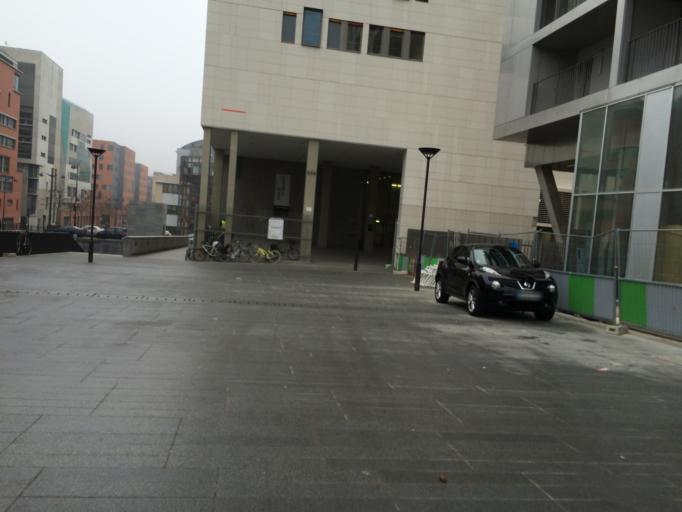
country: FR
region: Ile-de-France
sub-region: Departement du Val-de-Marne
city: Ivry-sur-Seine
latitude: 48.8271
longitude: 2.3804
